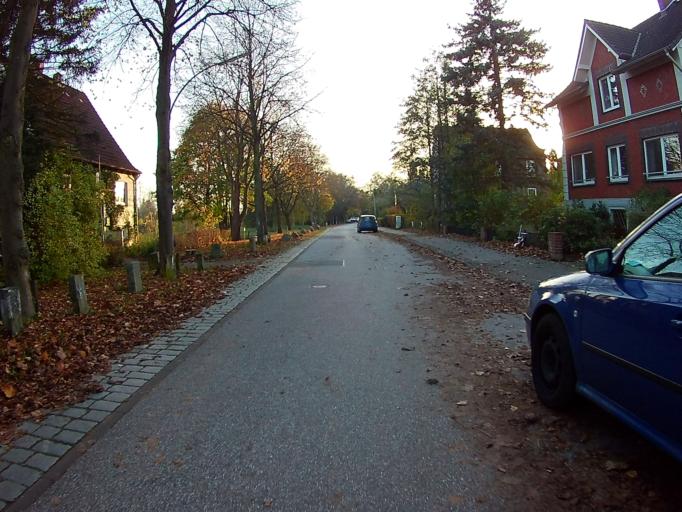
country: DE
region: Hamburg
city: Harburg
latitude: 53.4853
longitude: 9.9332
